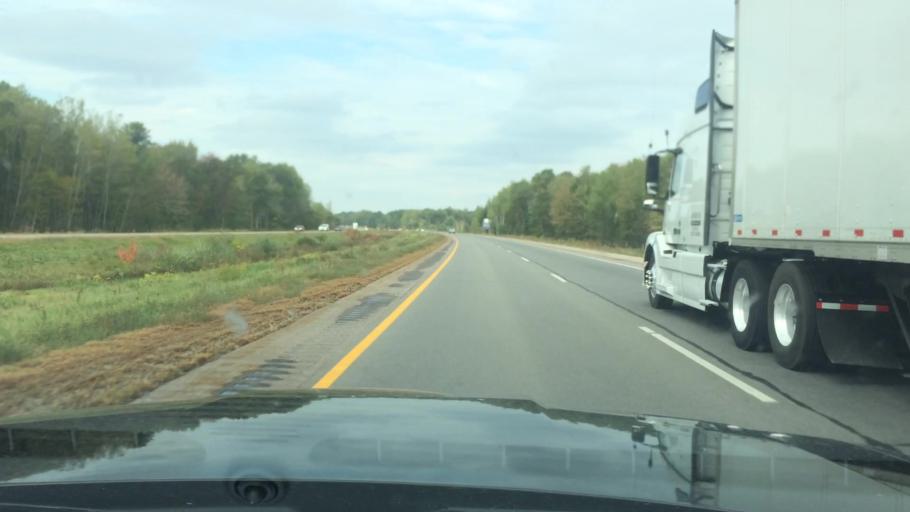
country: US
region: Wisconsin
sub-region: Marathon County
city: Mosinee
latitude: 44.7140
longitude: -89.6601
